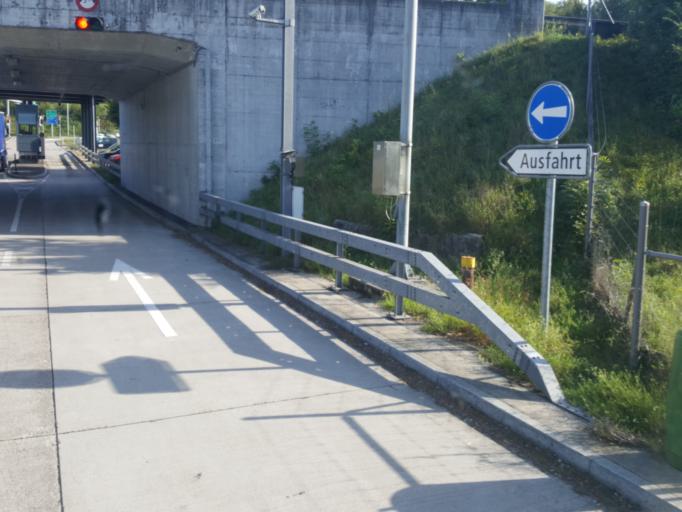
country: CH
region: Aargau
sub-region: Bezirk Rheinfelden
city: Kaiseraugst
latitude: 47.5455
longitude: 7.7567
